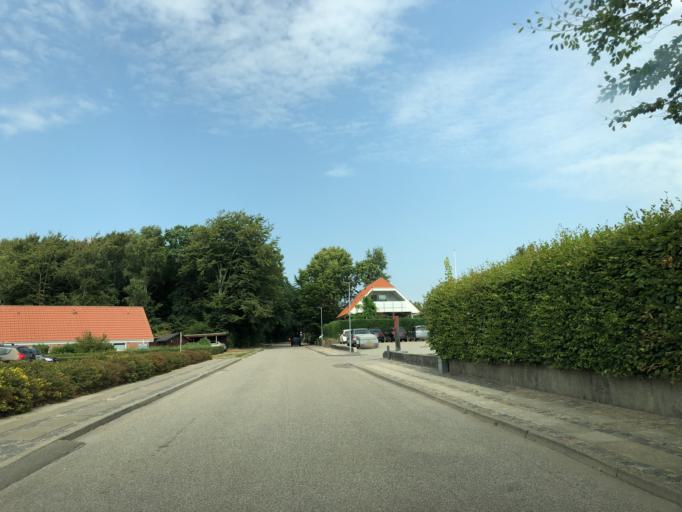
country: DK
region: Central Jutland
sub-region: Ringkobing-Skjern Kommune
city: Tarm
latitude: 55.9108
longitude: 8.5230
